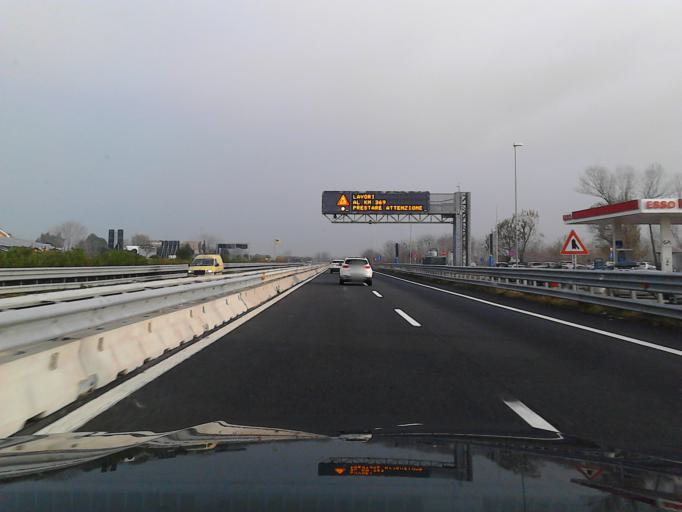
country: IT
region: Abruzzo
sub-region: Provincia di Pescara
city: San Martino Bassa
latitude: 42.5309
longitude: 14.1247
